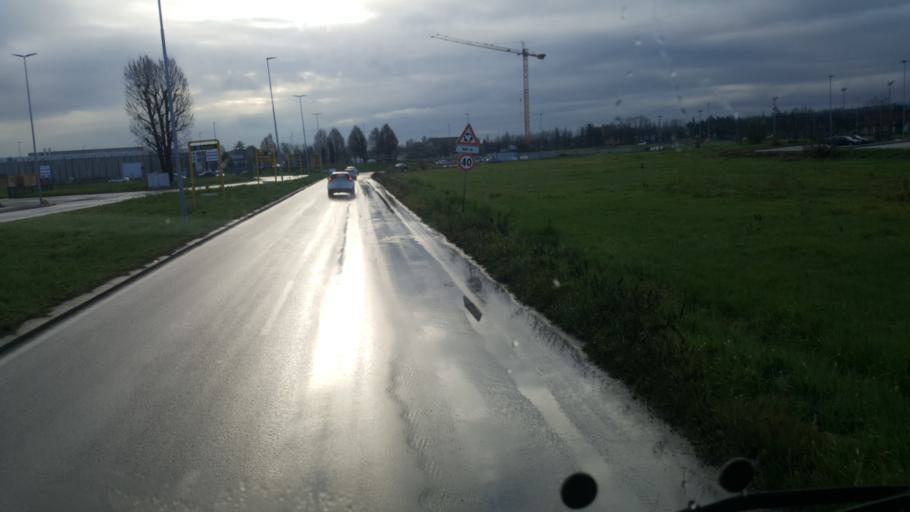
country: IT
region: Emilia-Romagna
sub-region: Provincia di Modena
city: Sassuolo
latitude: 44.5654
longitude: 10.7900
